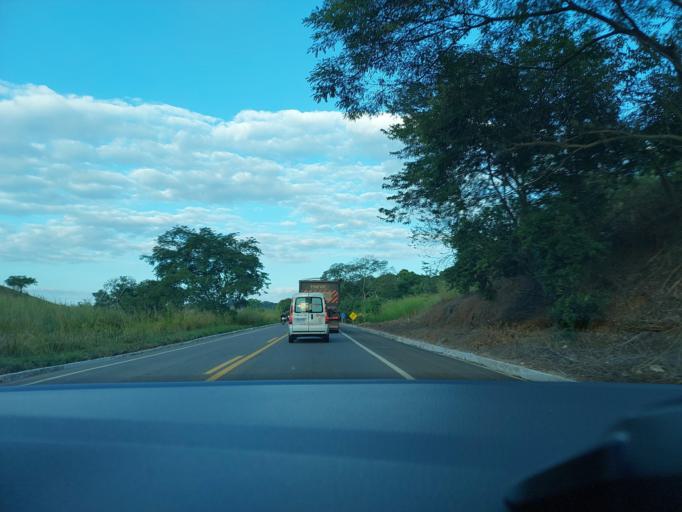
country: BR
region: Minas Gerais
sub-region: Muriae
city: Muriae
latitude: -21.1368
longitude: -42.1809
